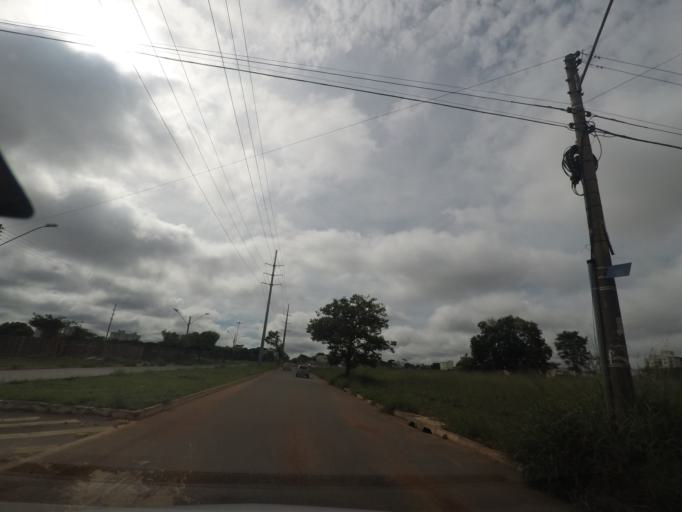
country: BR
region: Goias
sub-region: Goiania
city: Goiania
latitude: -16.7410
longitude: -49.3162
